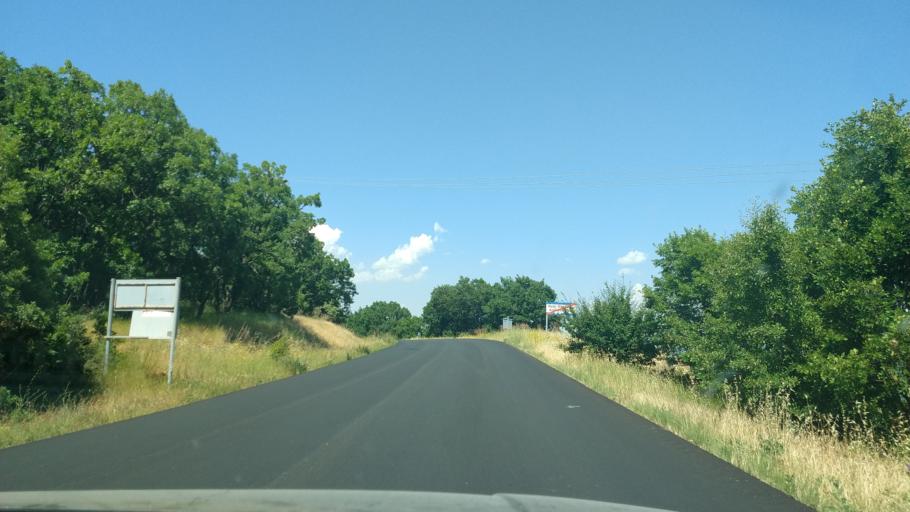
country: GR
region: West Macedonia
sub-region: Nomos Grevenon
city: Grevena
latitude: 39.9894
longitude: 21.5027
